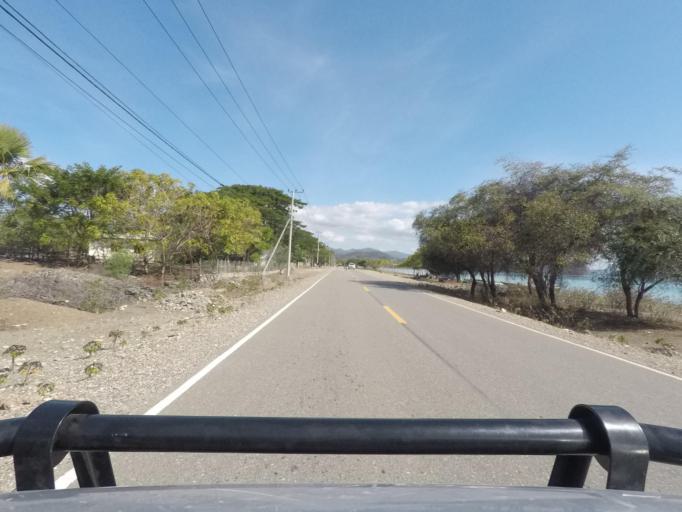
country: ID
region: East Nusa Tenggara
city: Atambua
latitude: -8.9320
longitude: 124.9808
